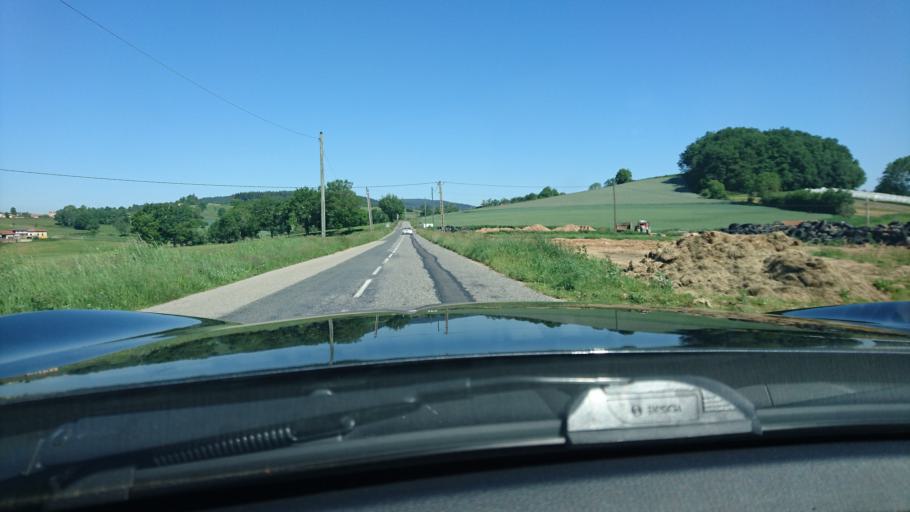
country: FR
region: Rhone-Alpes
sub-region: Departement du Rhone
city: Montrottier
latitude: 45.8047
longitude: 4.4261
